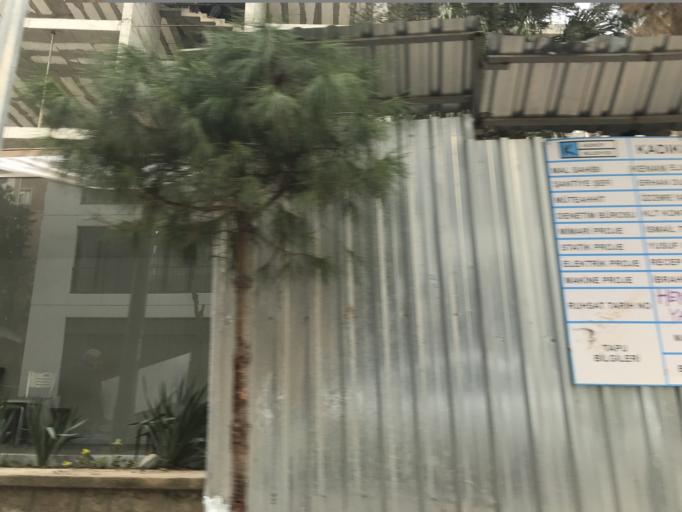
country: TR
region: Istanbul
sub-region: Atasehir
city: Atasehir
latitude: 40.9604
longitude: 29.0998
